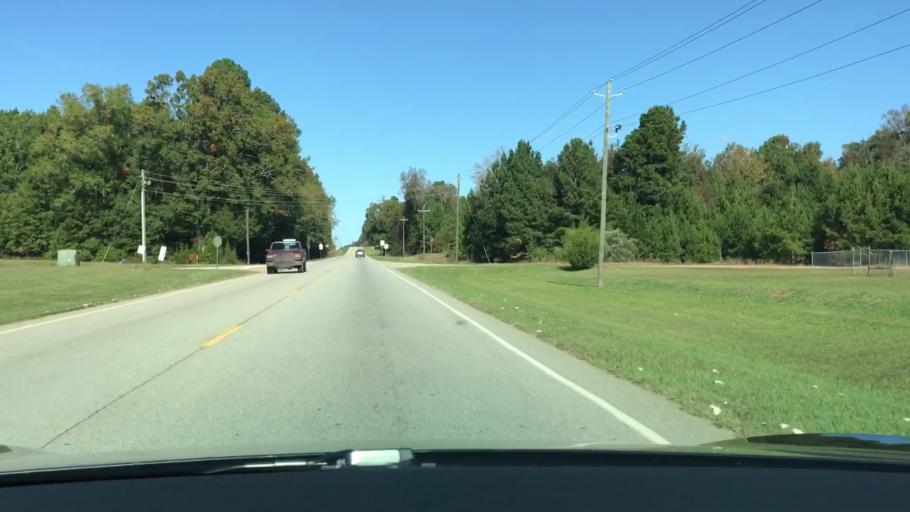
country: US
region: Georgia
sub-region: Warren County
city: West Warrenton
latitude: 33.4188
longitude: -82.6790
